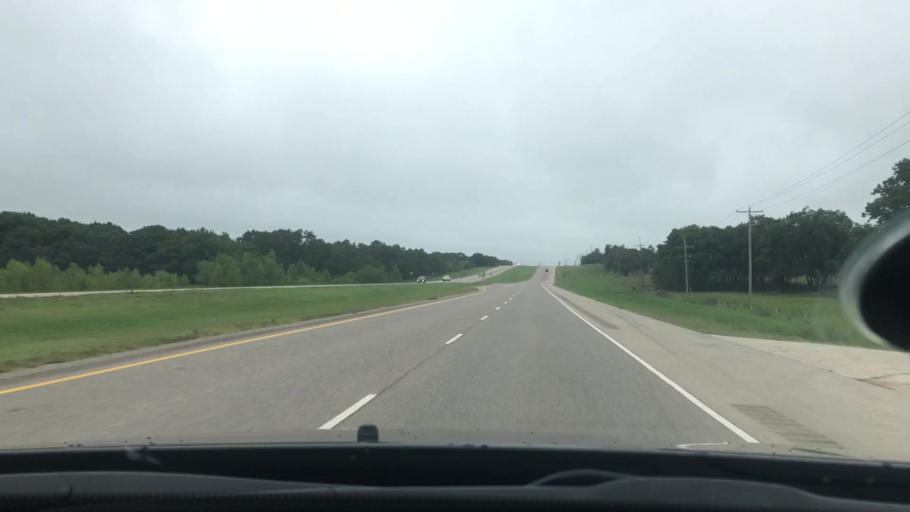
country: US
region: Oklahoma
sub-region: Seminole County
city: Seminole
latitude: 35.3384
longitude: -96.6714
